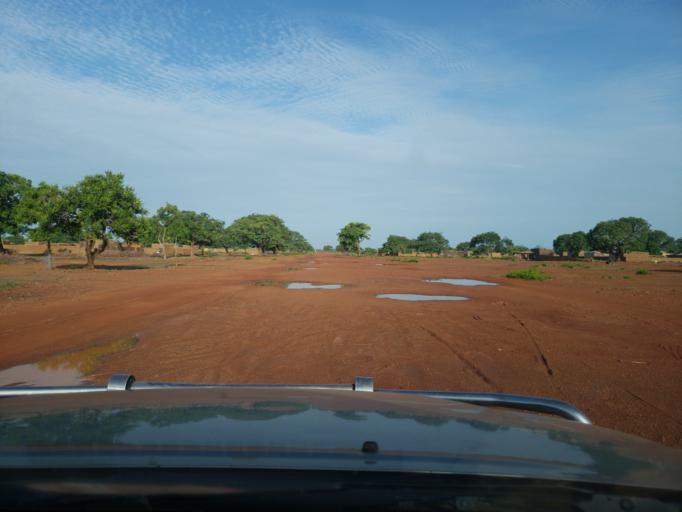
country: ML
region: Sikasso
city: Koutiala
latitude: 12.4290
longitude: -5.6173
